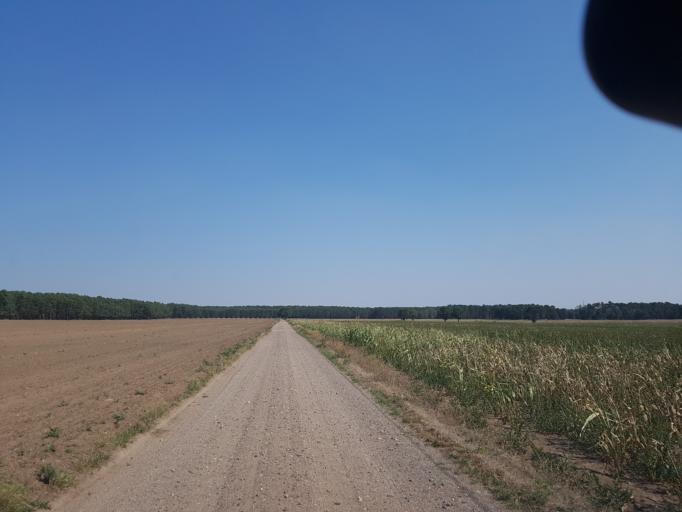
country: DE
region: Saxony-Anhalt
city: Coswig
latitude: 51.9761
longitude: 12.4372
